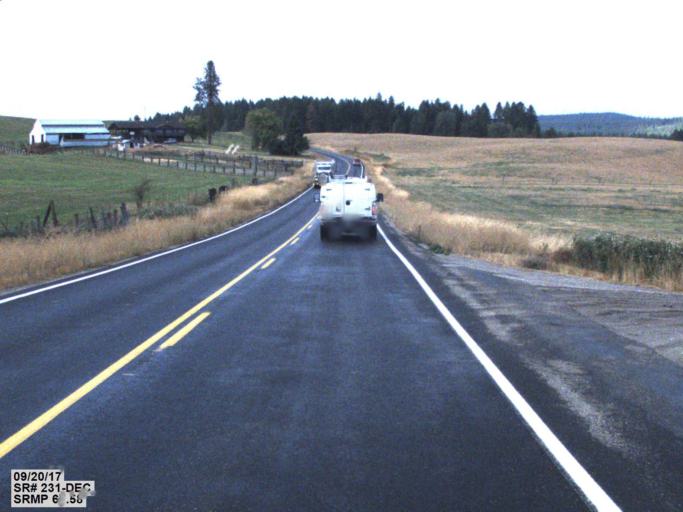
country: US
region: Washington
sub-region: Stevens County
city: Chewelah
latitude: 48.1215
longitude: -117.7511
